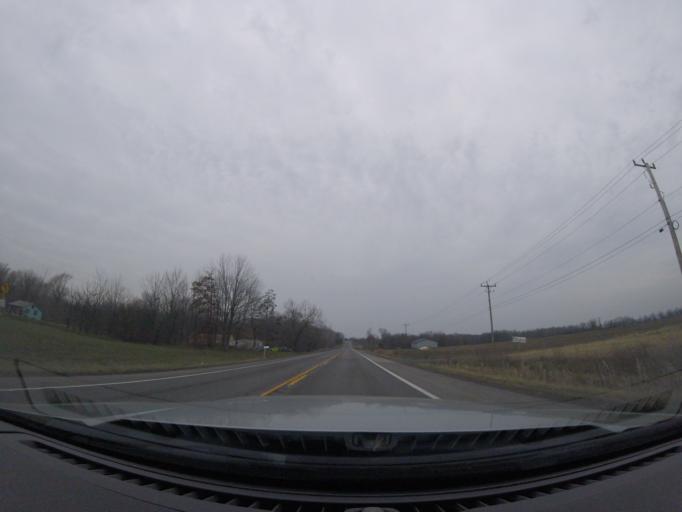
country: US
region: New York
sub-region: Yates County
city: Penn Yan
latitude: 42.6659
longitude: -76.9456
